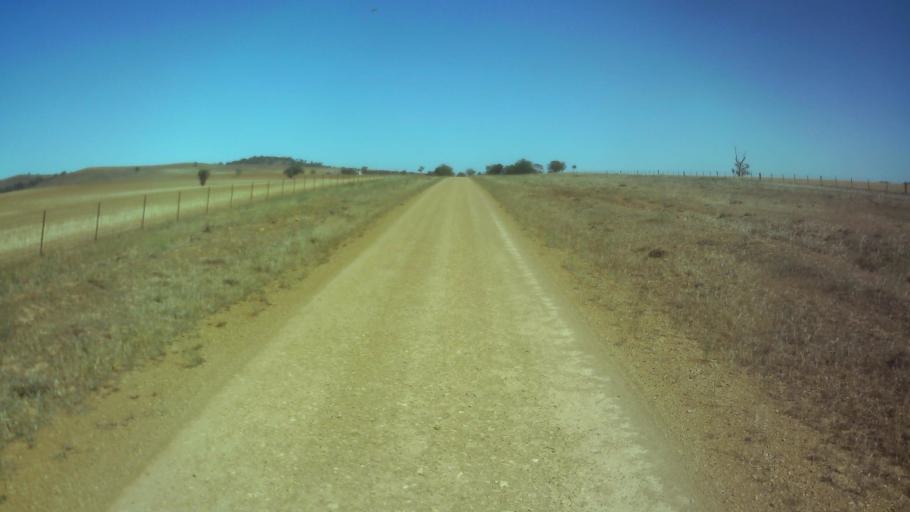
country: AU
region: New South Wales
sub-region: Weddin
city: Grenfell
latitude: -33.9664
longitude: 148.3115
